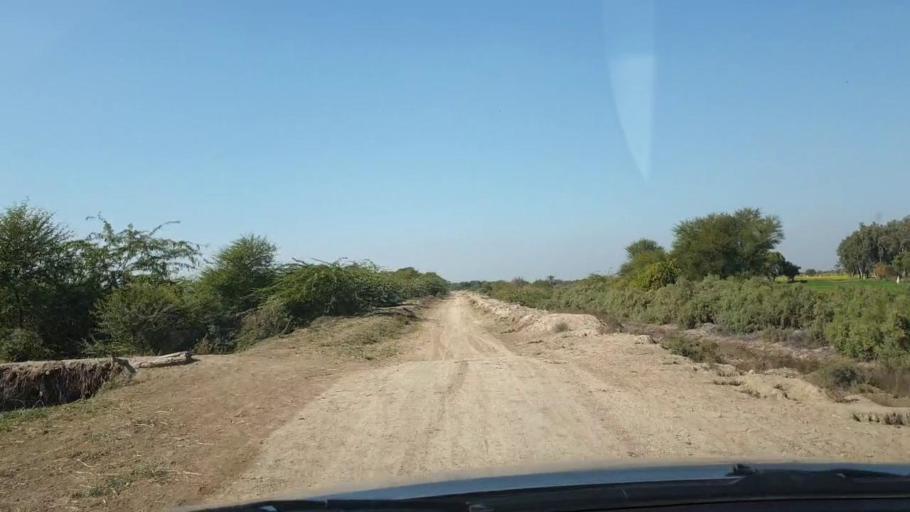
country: PK
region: Sindh
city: Jhol
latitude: 25.9235
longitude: 68.9579
